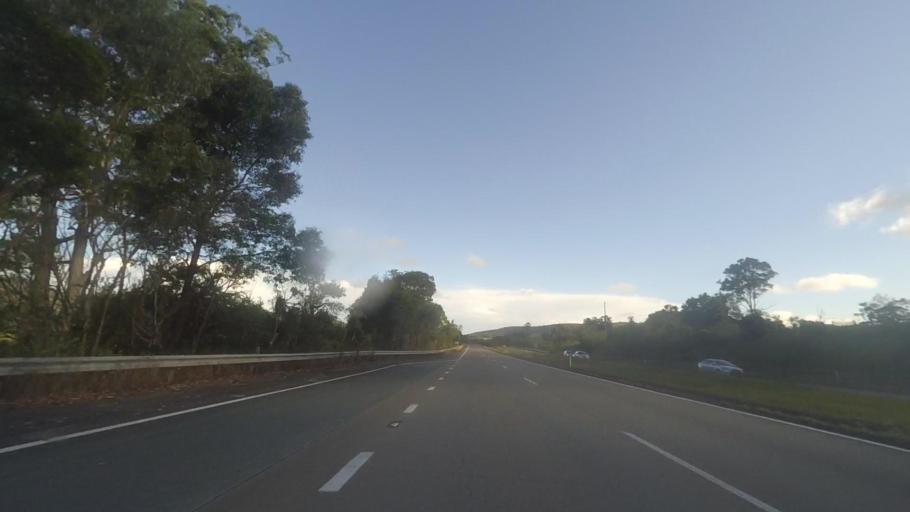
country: AU
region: New South Wales
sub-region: Great Lakes
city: Nabiac
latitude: -32.2545
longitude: 152.3240
